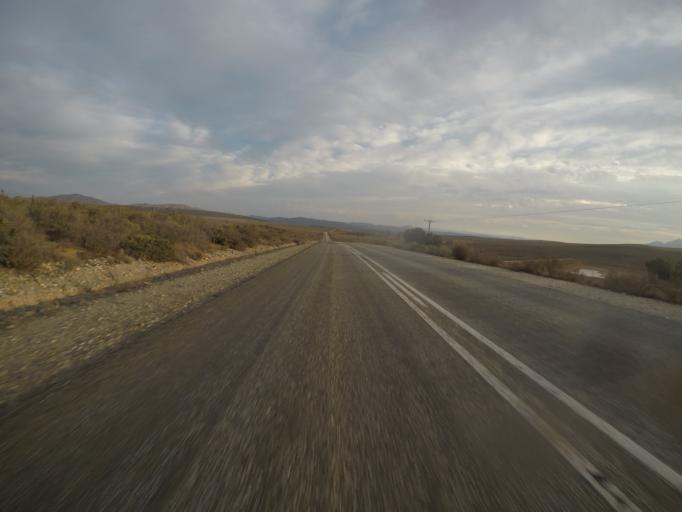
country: ZA
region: Eastern Cape
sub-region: Cacadu District Municipality
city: Willowmore
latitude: -33.5922
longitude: 23.1523
